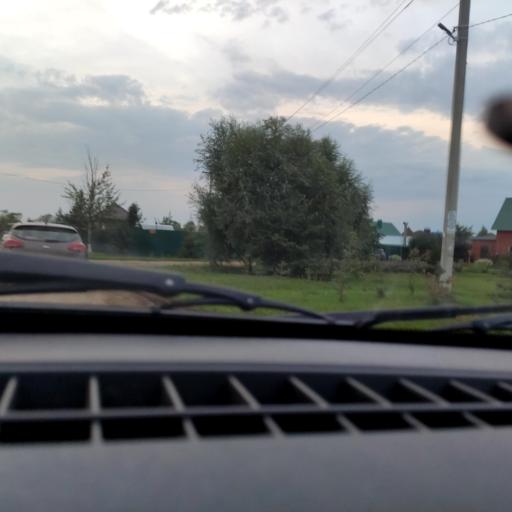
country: RU
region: Bashkortostan
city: Ufa
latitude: 54.6444
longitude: 55.9148
